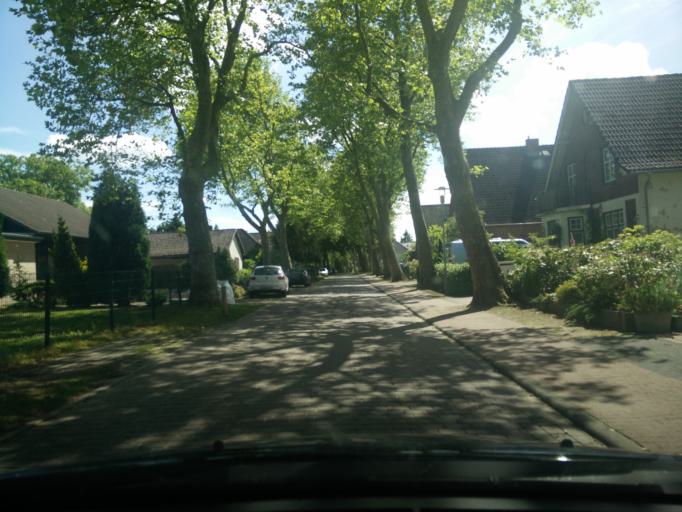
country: DE
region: Schleswig-Holstein
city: Prisdorf
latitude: 53.6778
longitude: 9.7612
